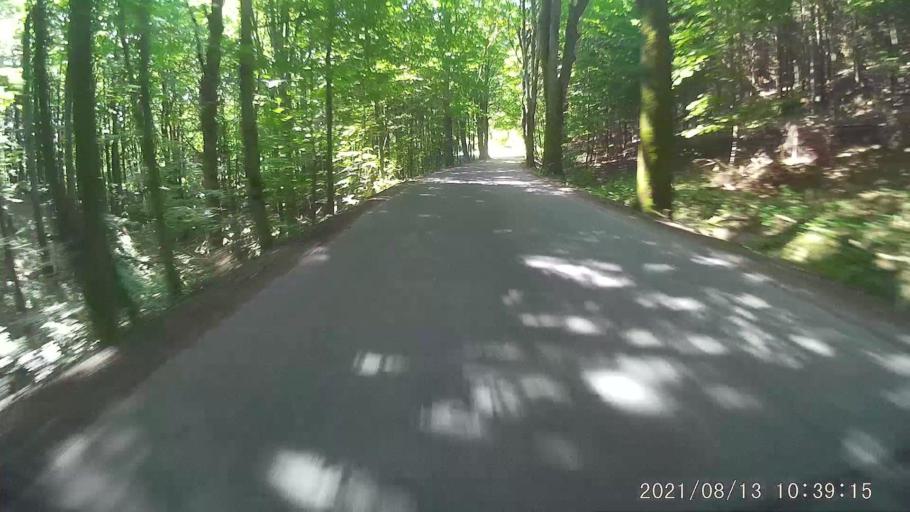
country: PL
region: Lower Silesian Voivodeship
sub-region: Powiat klodzki
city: Duszniki-Zdroj
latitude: 50.4439
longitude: 16.3432
